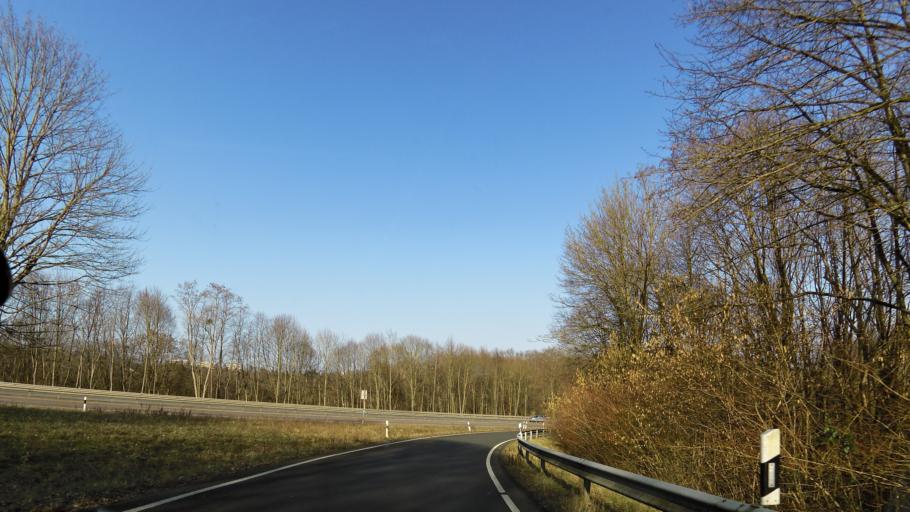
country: DE
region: Rheinland-Pfalz
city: Koblenz
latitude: 50.3294
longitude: 7.5679
